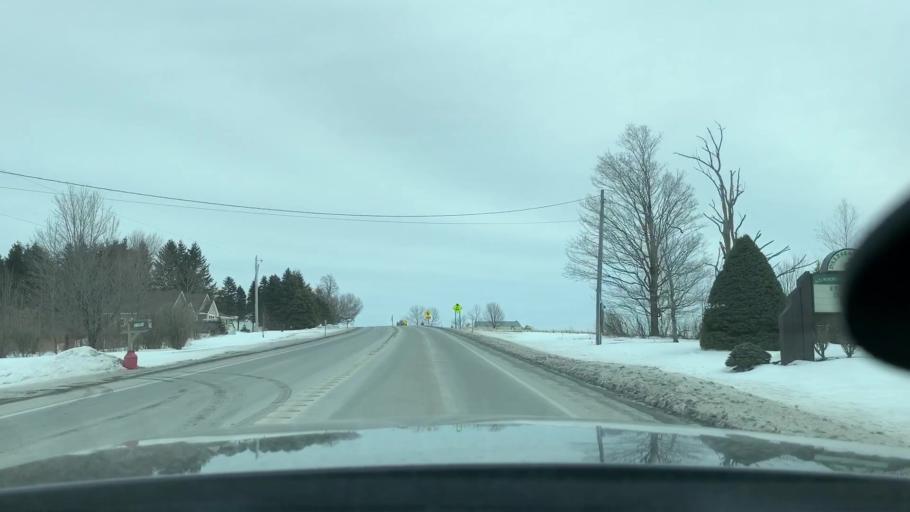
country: US
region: New York
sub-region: Oneida County
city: Utica
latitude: 43.0317
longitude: -75.1754
